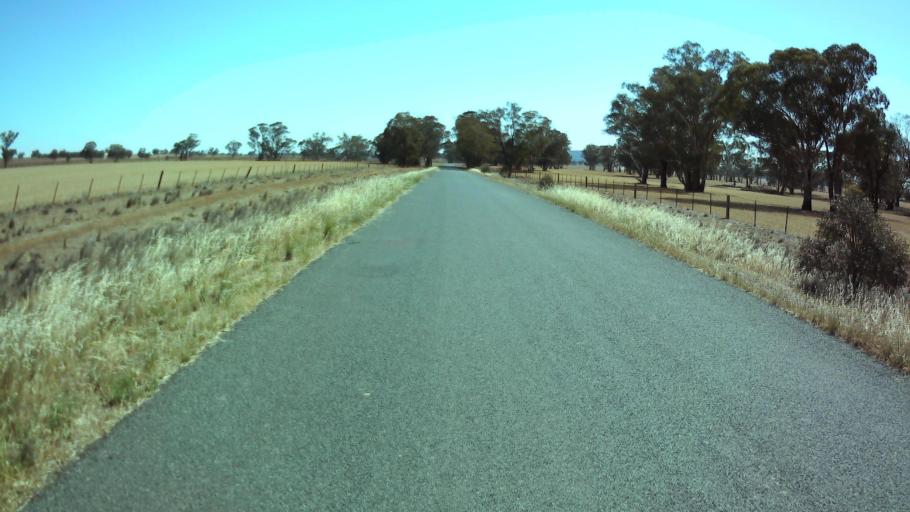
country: AU
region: New South Wales
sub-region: Weddin
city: Grenfell
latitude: -33.7327
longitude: 147.8873
